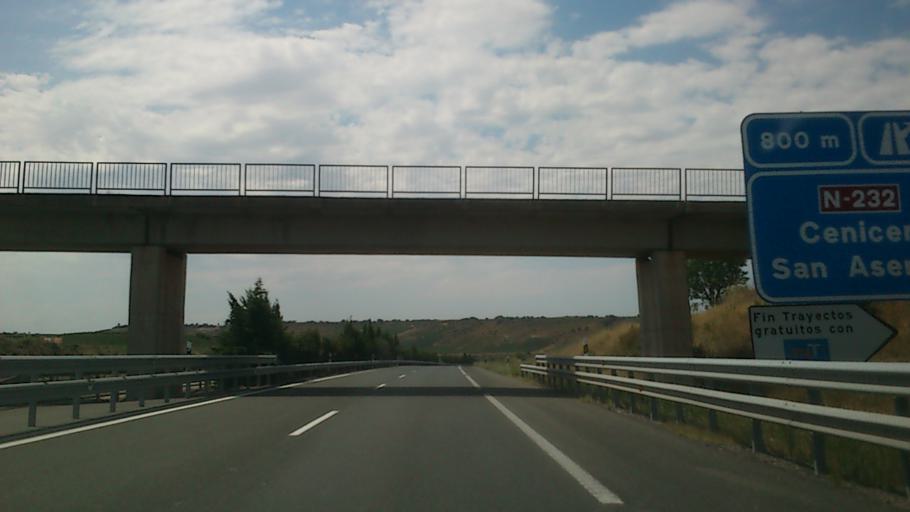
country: ES
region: La Rioja
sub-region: Provincia de La Rioja
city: Cenicero
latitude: 42.4610
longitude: -2.6324
